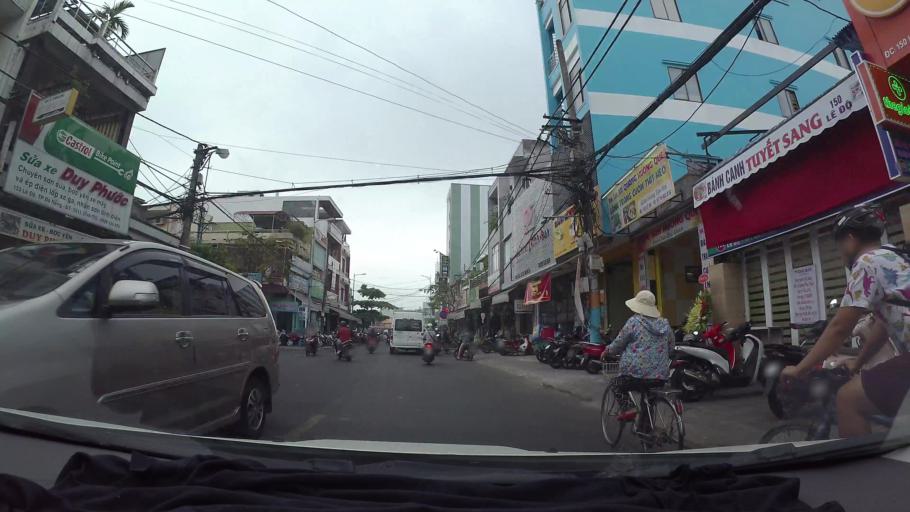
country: VN
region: Da Nang
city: Thanh Khe
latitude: 16.0668
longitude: 108.2016
